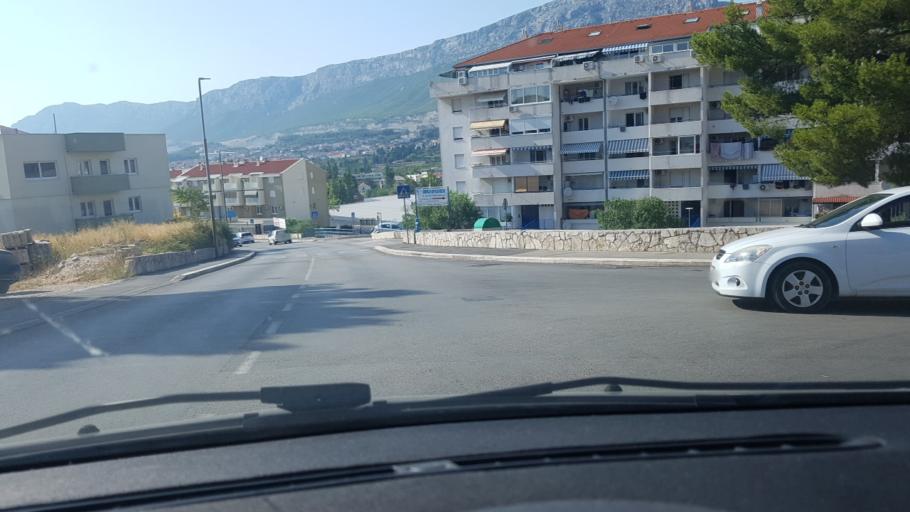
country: HR
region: Splitsko-Dalmatinska
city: Solin
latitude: 43.5317
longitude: 16.4918
